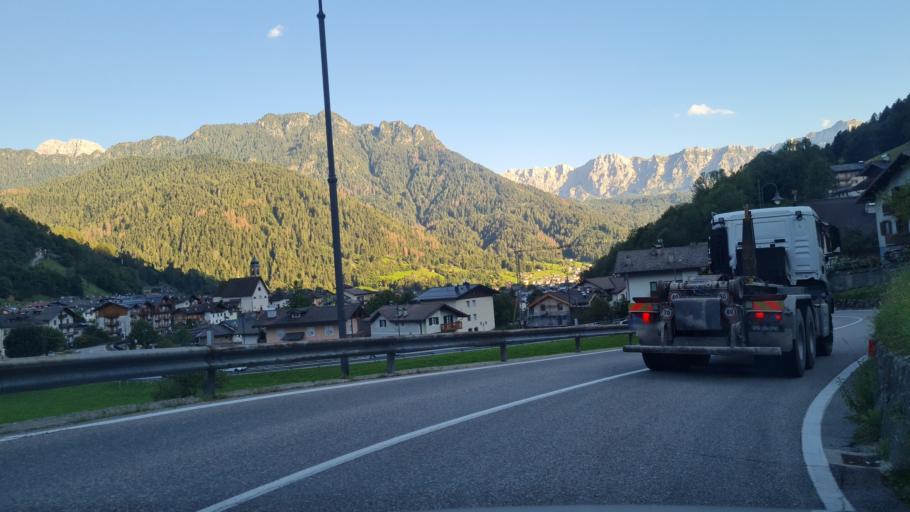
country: IT
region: Trentino-Alto Adige
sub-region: Provincia di Trento
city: Siror
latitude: 46.1907
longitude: 11.8262
